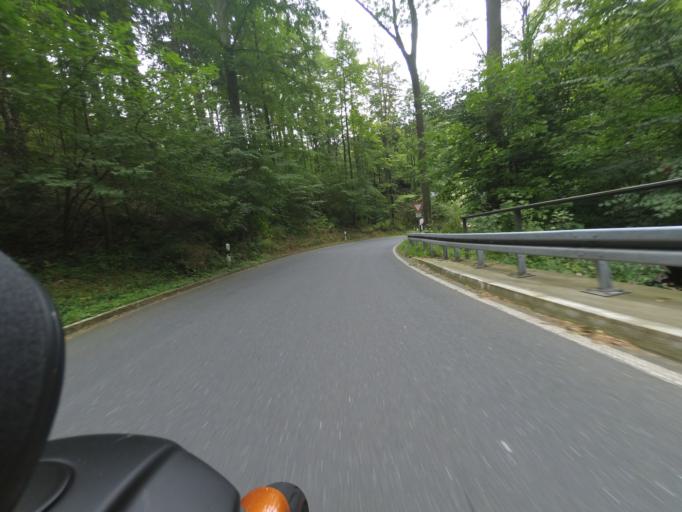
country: DE
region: Saxony
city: Glashutte
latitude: 50.8528
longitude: 13.7934
